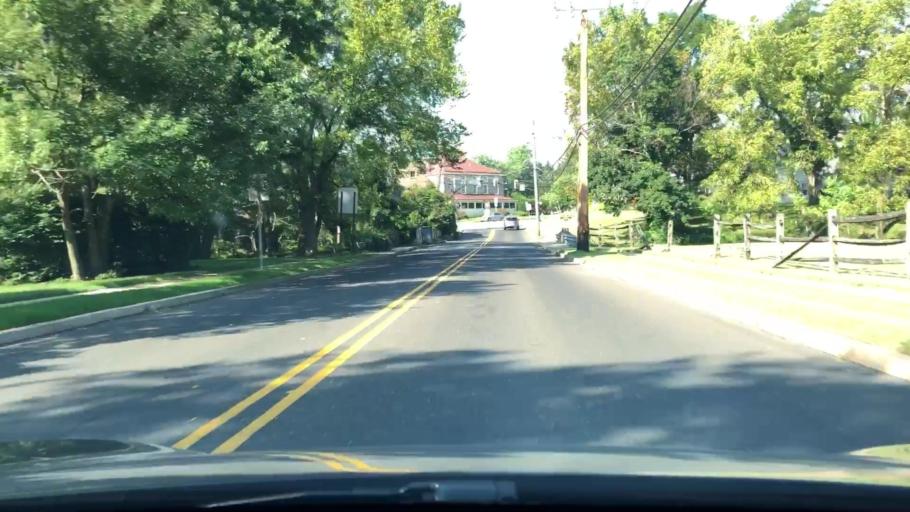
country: US
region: Pennsylvania
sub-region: Montgomery County
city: Dresher
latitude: 40.1556
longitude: -75.1740
